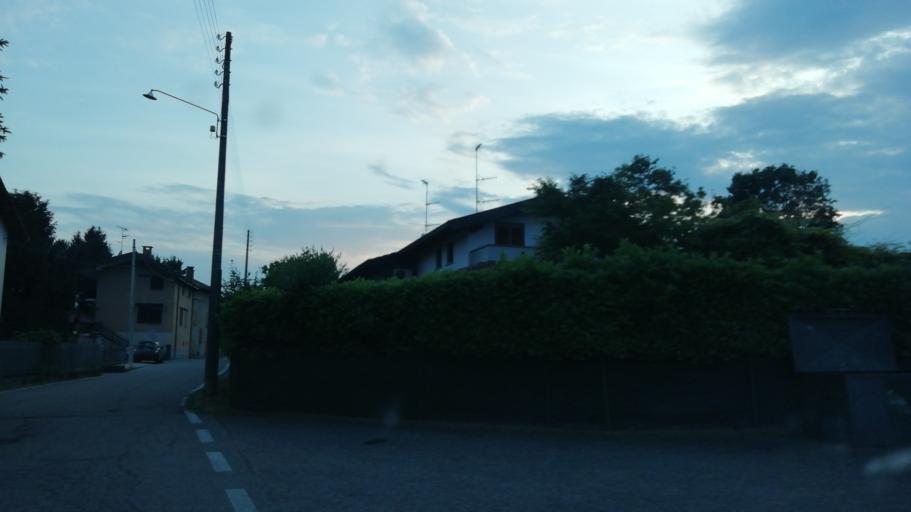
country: IT
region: Piedmont
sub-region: Provincia di Novara
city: Castelletto Sopra Ticino
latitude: 45.7072
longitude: 8.6252
